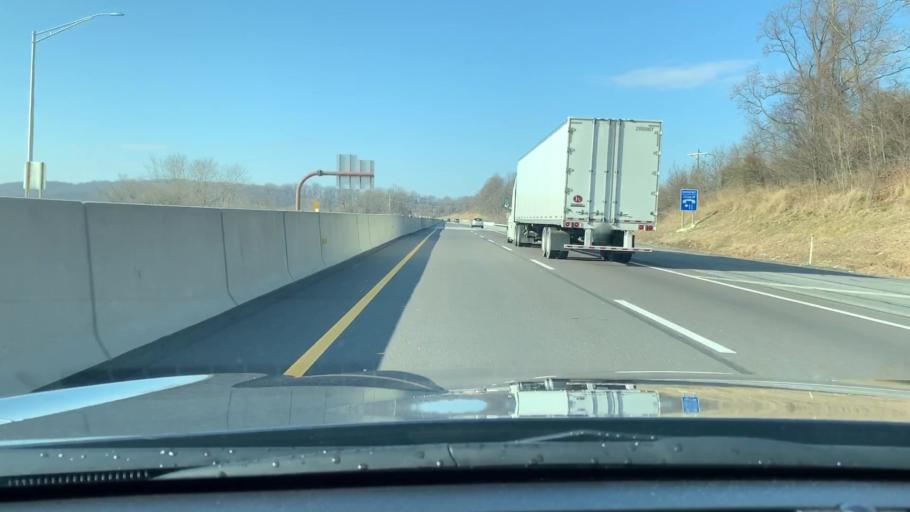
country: US
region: Pennsylvania
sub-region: Chester County
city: Malvern
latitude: 40.0767
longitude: -75.5361
